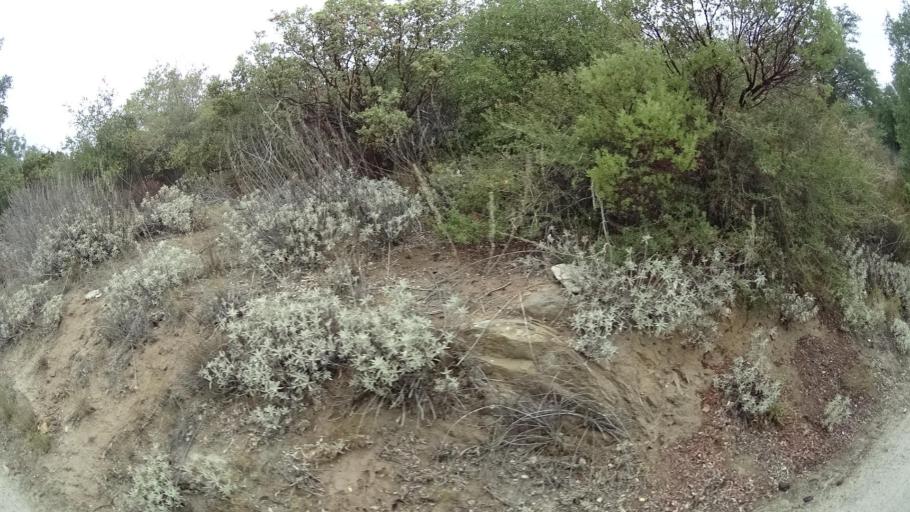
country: US
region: California
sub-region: San Diego County
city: Julian
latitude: 32.9946
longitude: -116.6531
